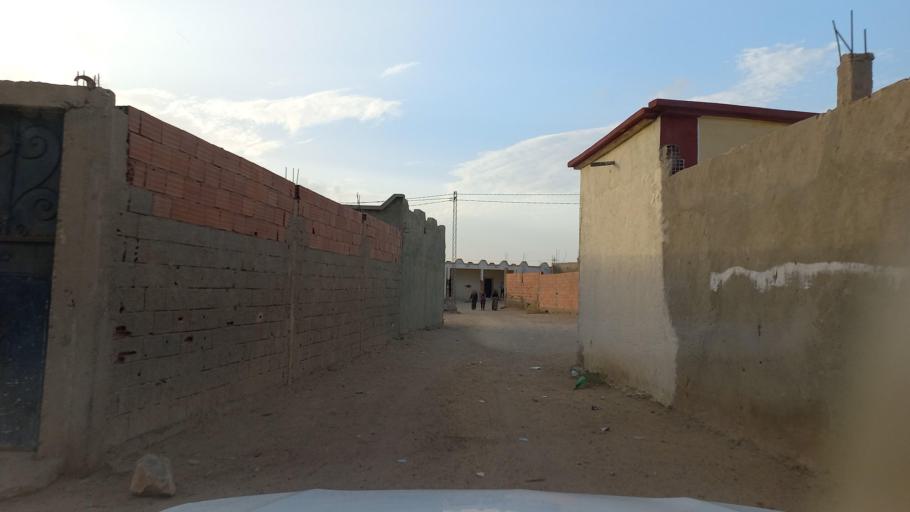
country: TN
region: Al Qasrayn
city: Kasserine
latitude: 35.2700
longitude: 9.0681
